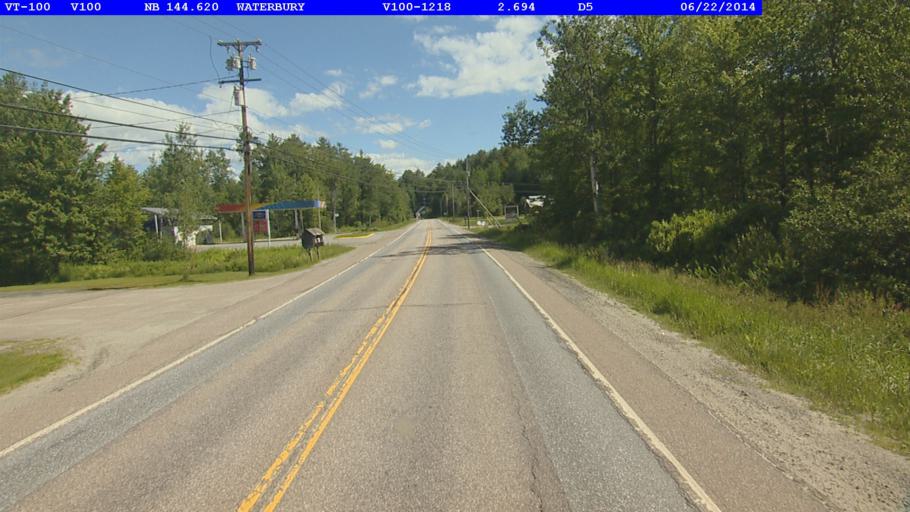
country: US
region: Vermont
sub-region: Washington County
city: Waterbury
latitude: 44.3696
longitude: -72.7279
